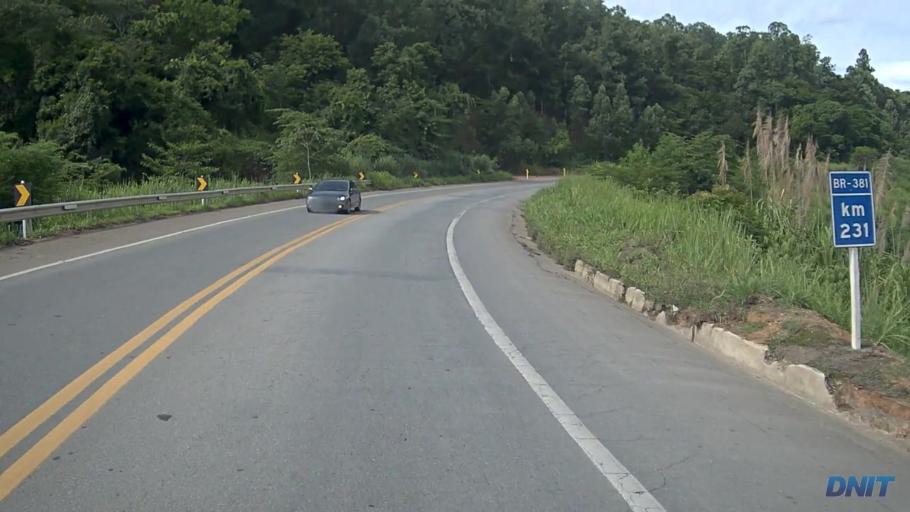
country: BR
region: Minas Gerais
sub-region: Ipaba
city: Ipaba
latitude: -19.3253
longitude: -42.4188
